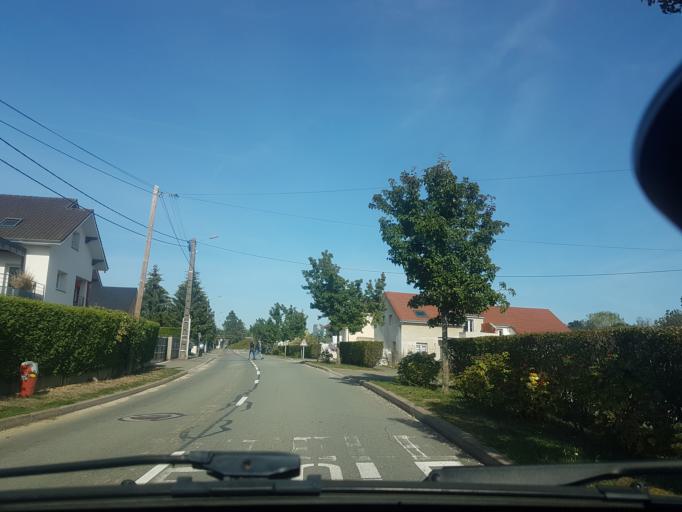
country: FR
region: Franche-Comte
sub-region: Territoire de Belfort
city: Offemont
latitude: 47.6568
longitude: 6.9047
